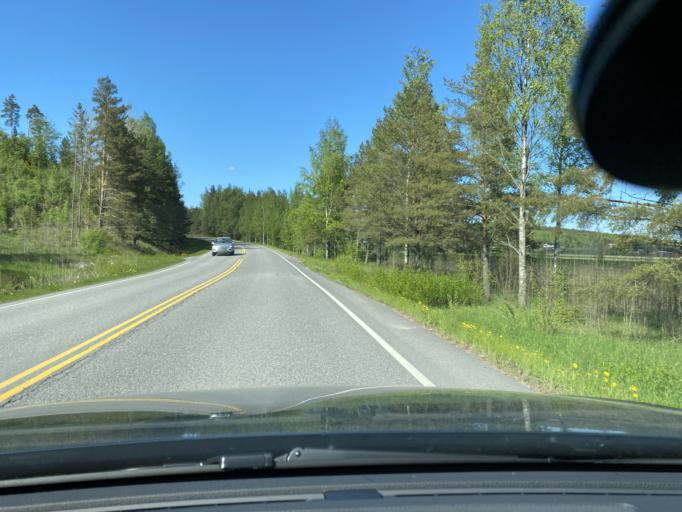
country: FI
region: Varsinais-Suomi
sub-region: Turku
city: Sauvo
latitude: 60.3650
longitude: 22.6742
